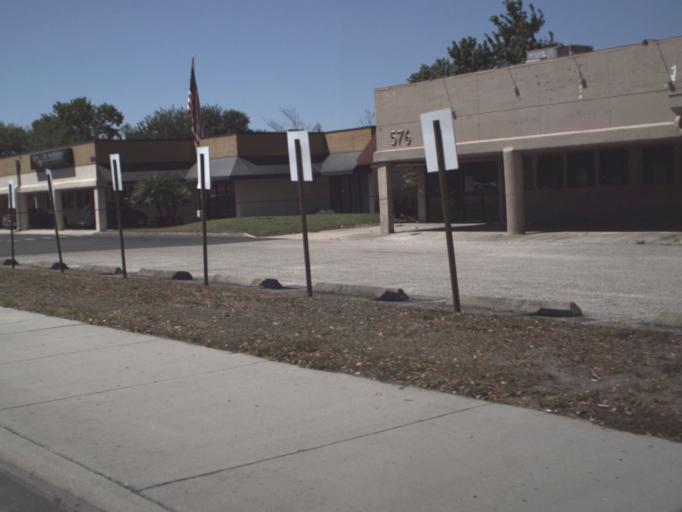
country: US
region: Florida
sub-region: Orange County
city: Azalea Park
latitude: 28.5513
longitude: -81.3108
